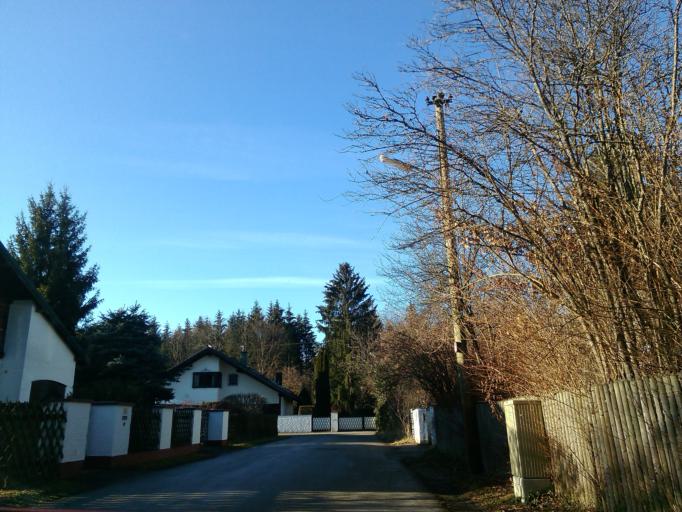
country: DE
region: Bavaria
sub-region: Upper Bavaria
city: Gauting
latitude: 48.0541
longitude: 11.3608
